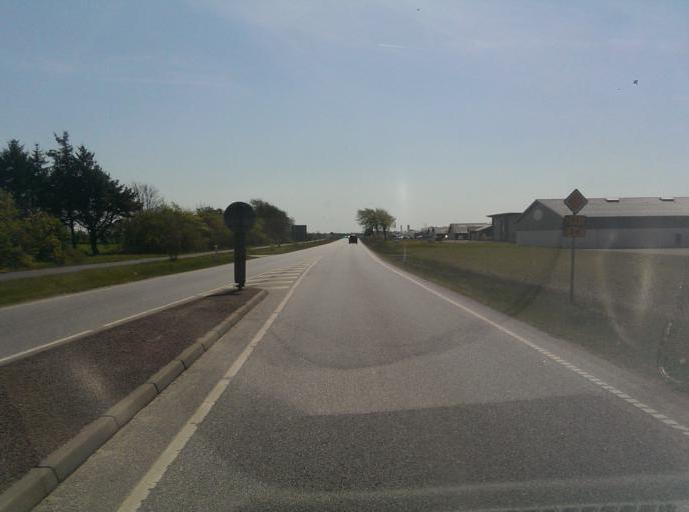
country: DK
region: South Denmark
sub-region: Esbjerg Kommune
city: Ribe
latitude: 55.3610
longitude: 8.7719
